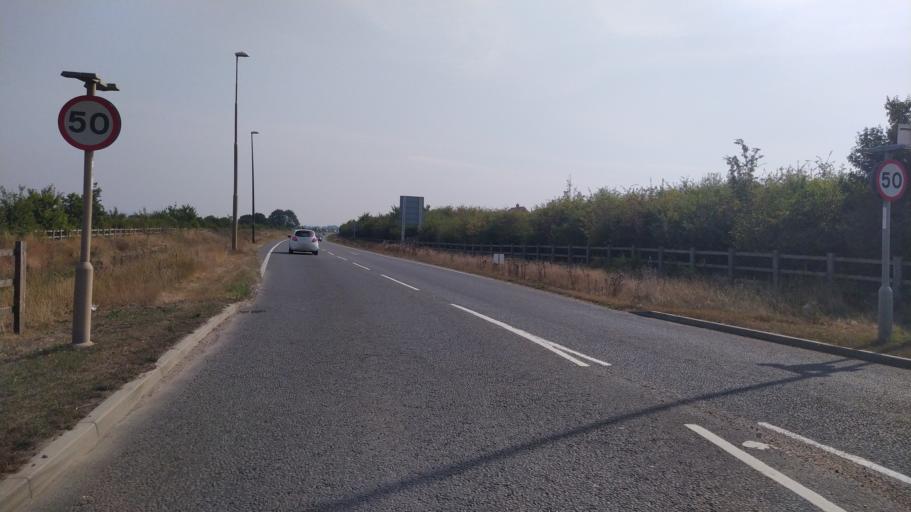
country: GB
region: England
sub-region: West Sussex
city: Bognor Regis
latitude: 50.8059
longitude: -0.6993
